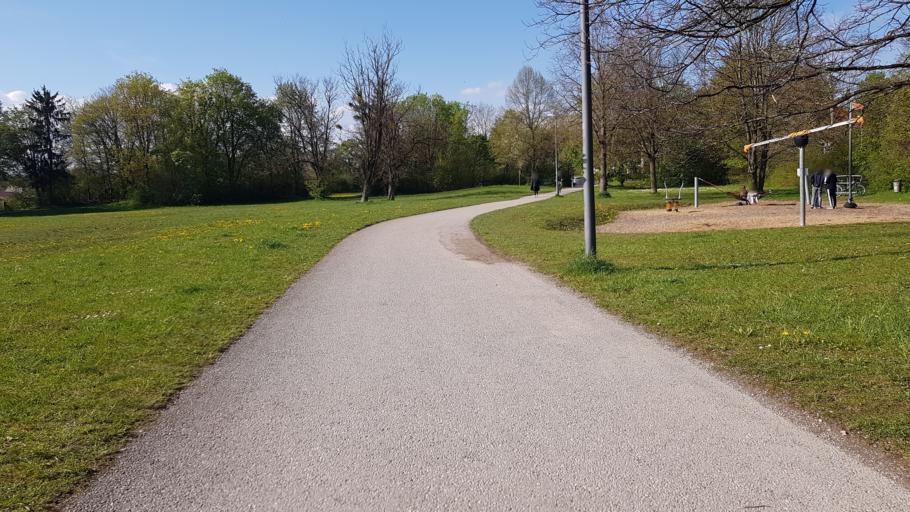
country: DE
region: Bavaria
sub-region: Upper Bavaria
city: Pasing
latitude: 48.1690
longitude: 11.5017
